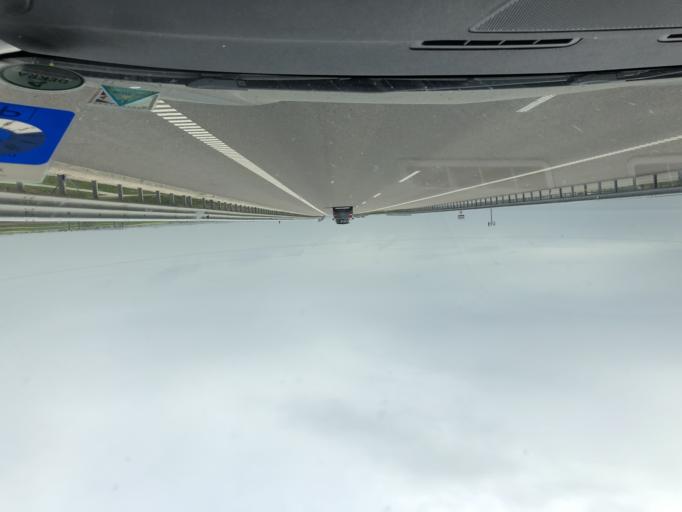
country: PL
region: Subcarpathian Voivodeship
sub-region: Powiat jaroslawski
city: Sosnica
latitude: 49.9142
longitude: 22.8503
